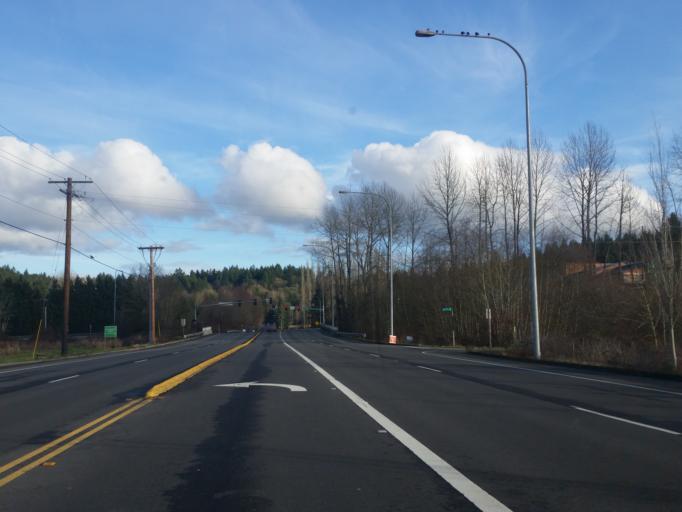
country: US
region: Washington
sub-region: King County
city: Redmond
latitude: 47.7112
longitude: -122.1343
